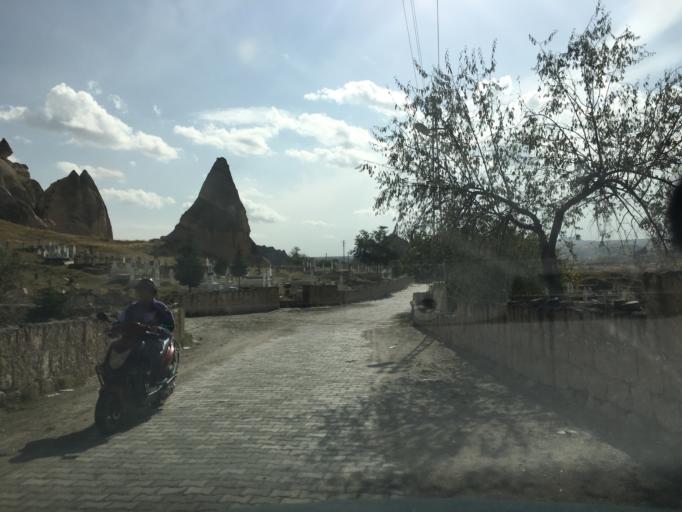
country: TR
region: Nevsehir
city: Goereme
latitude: 38.6657
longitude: 34.8413
